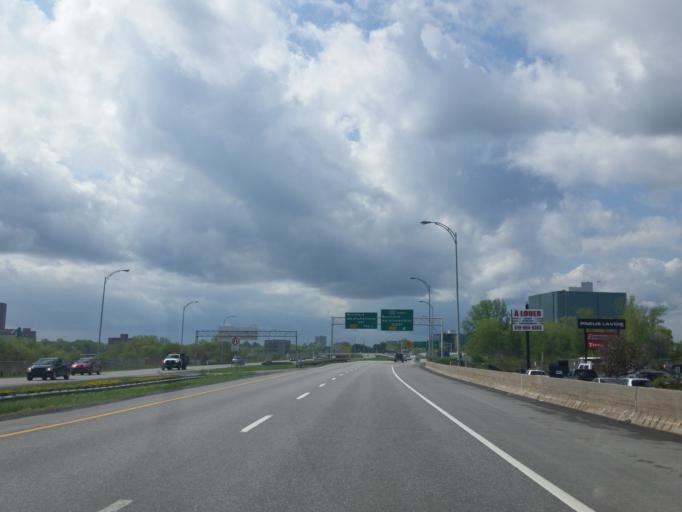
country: CA
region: Ontario
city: Ottawa
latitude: 45.4380
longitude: -75.7266
